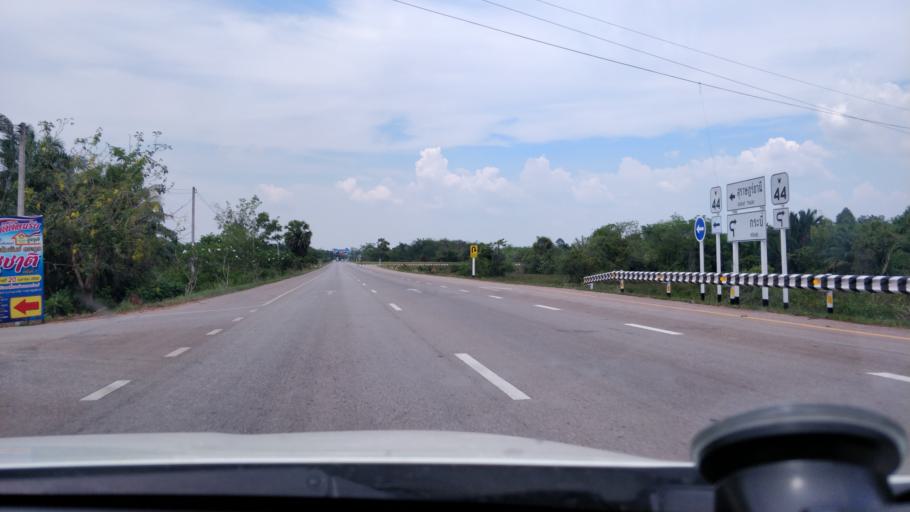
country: TH
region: Surat Thani
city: Ban Na Doem
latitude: 8.9254
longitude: 99.2558
